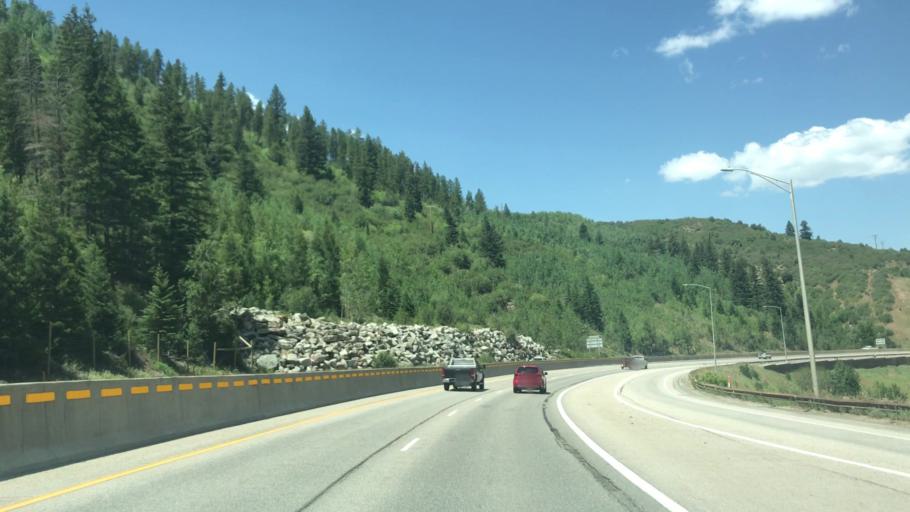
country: US
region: Colorado
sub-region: Eagle County
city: Minturn
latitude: 39.6099
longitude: -106.4565
